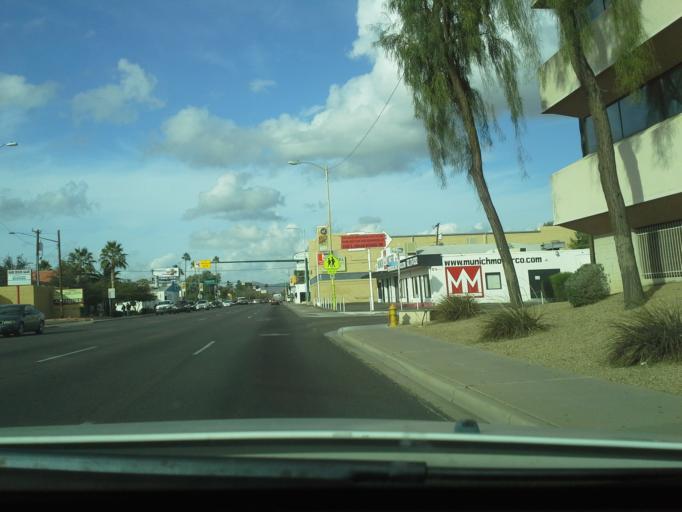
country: US
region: Arizona
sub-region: Maricopa County
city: Phoenix
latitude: 33.5072
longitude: -112.0824
